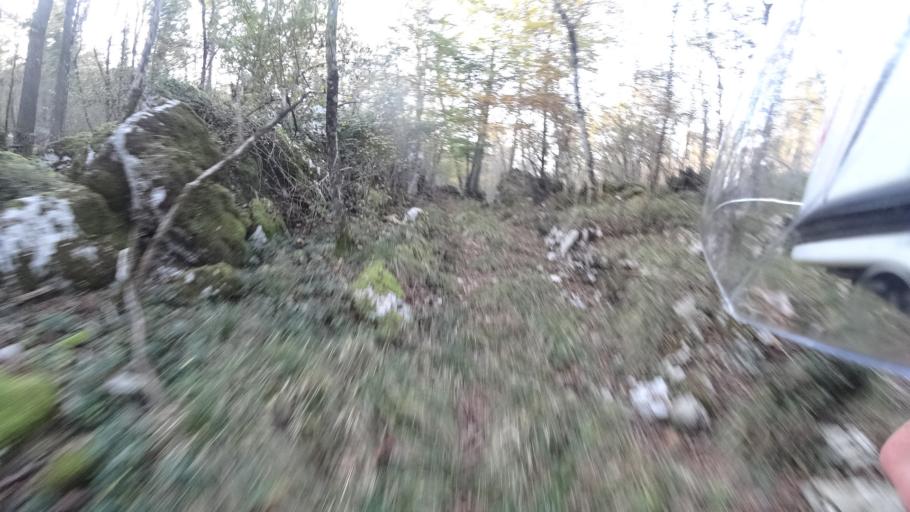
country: HR
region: Primorsko-Goranska
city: Kastav
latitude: 45.4022
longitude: 14.3180
